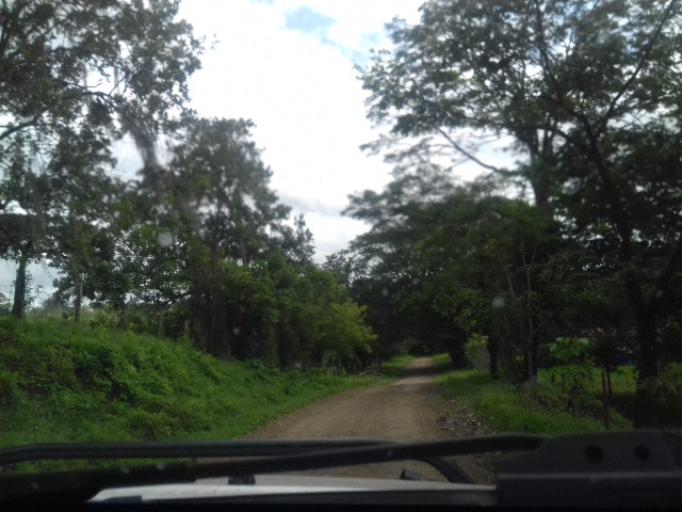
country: NI
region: Matagalpa
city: Matiguas
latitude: 12.8660
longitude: -85.3870
